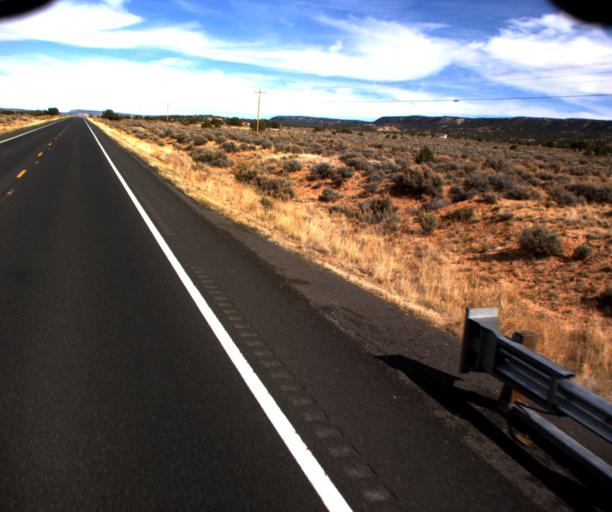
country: US
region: Arizona
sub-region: Navajo County
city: Kayenta
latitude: 36.5079
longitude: -110.6069
